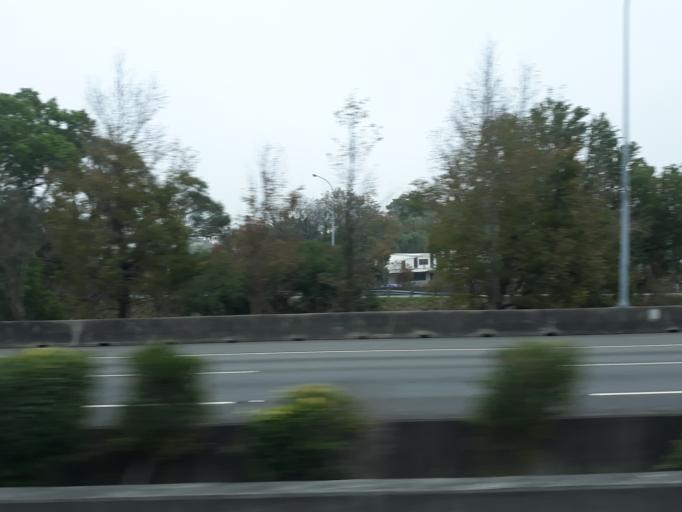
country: TW
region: Taiwan
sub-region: Miaoli
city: Miaoli
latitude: 24.5231
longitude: 120.8184
